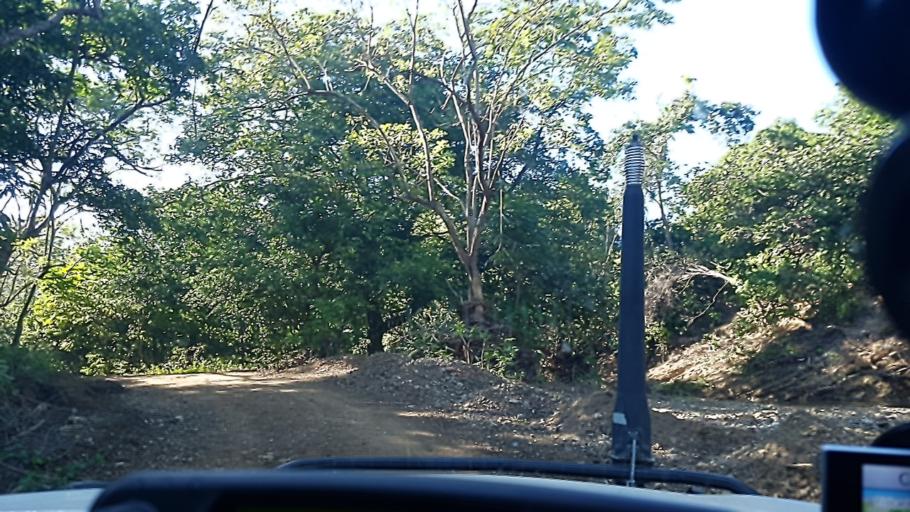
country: NI
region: Rivas
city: Tola
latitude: 11.5419
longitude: -86.1191
